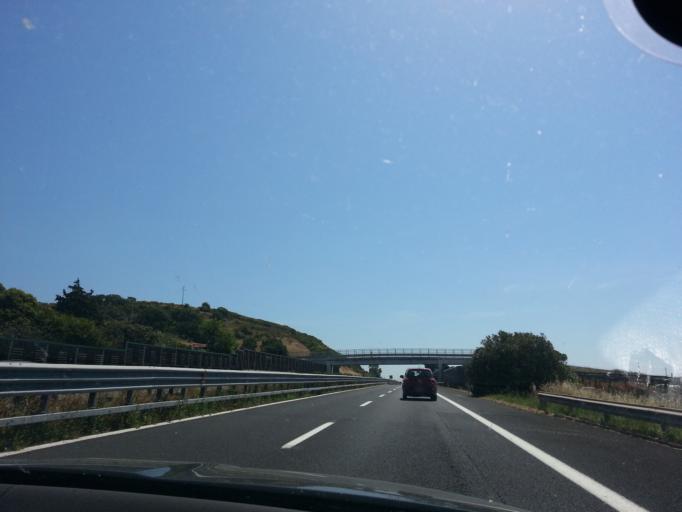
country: IT
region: Latium
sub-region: Citta metropolitana di Roma Capitale
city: Santa Marinella
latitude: 42.0443
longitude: 11.8975
